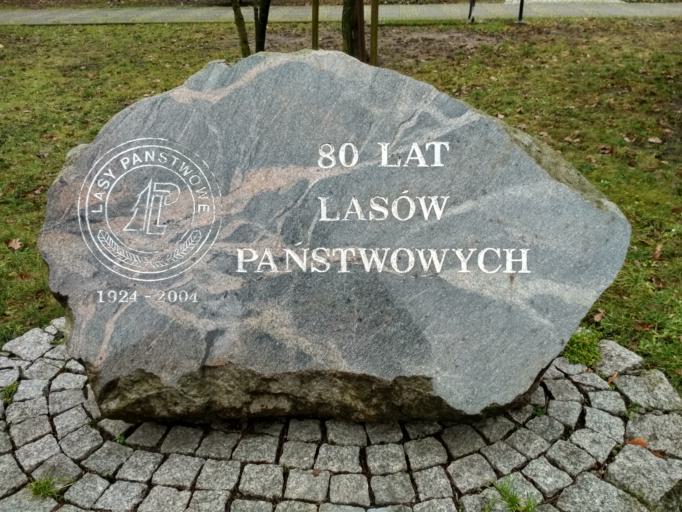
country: PL
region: Lubusz
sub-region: Zielona Gora
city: Zielona Gora
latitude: 51.9440
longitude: 15.5119
